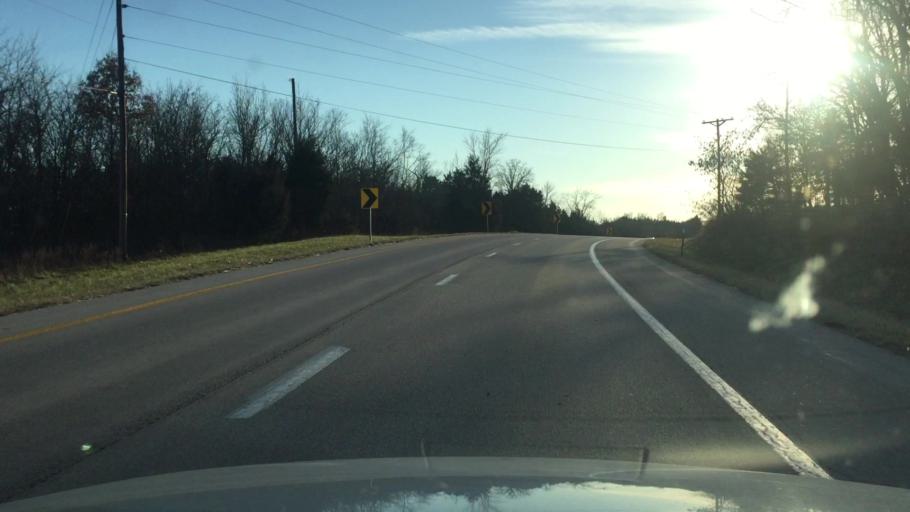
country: US
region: Missouri
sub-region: Cole County
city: Wardsville
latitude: 38.4272
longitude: -92.3258
